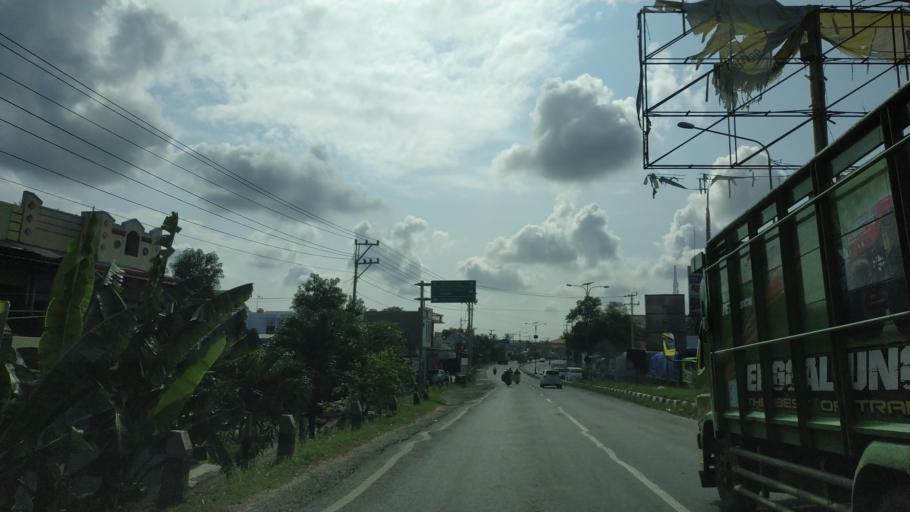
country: ID
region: Central Java
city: Comal
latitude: -6.8992
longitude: 109.5256
